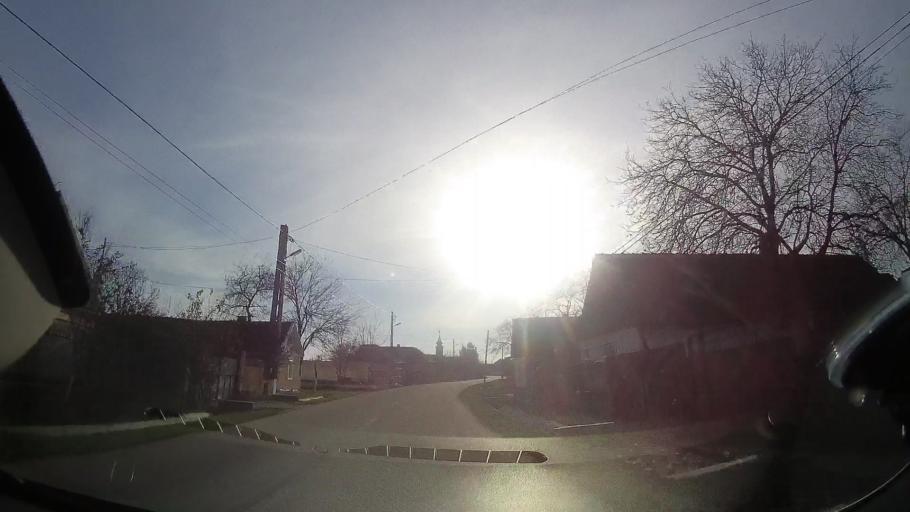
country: RO
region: Bihor
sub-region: Comuna Sarbi
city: Sarbi
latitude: 47.2095
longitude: 22.1315
